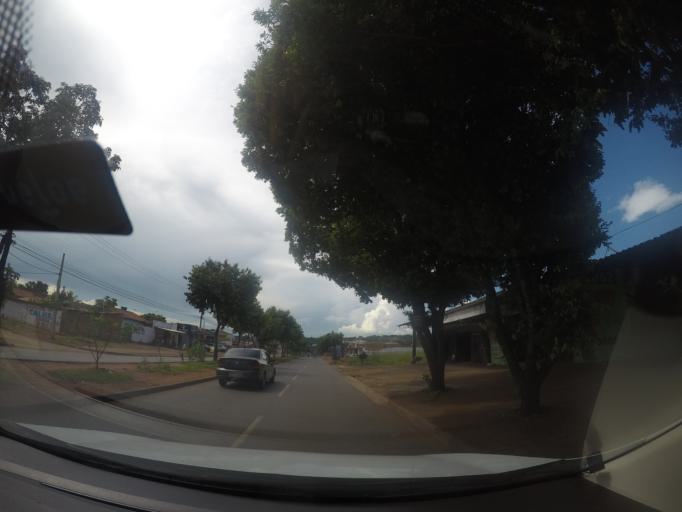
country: BR
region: Goias
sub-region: Trindade
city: Trindade
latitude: -16.6758
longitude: -49.3858
